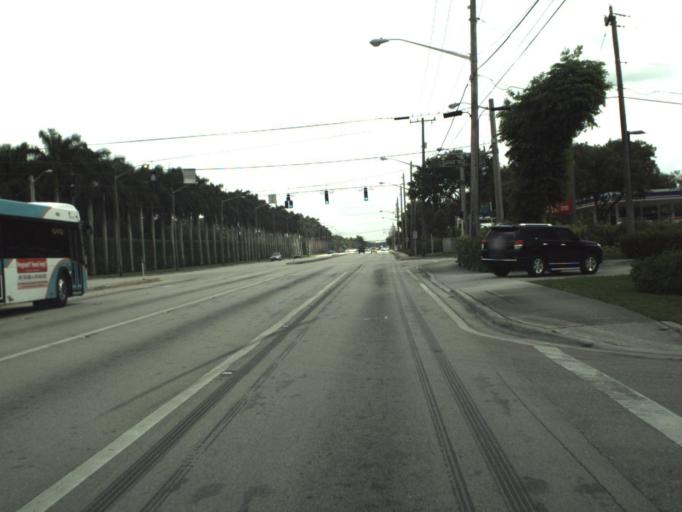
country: US
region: Florida
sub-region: Palm Beach County
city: Lake Clarke Shores
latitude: 26.6657
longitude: -80.0880
